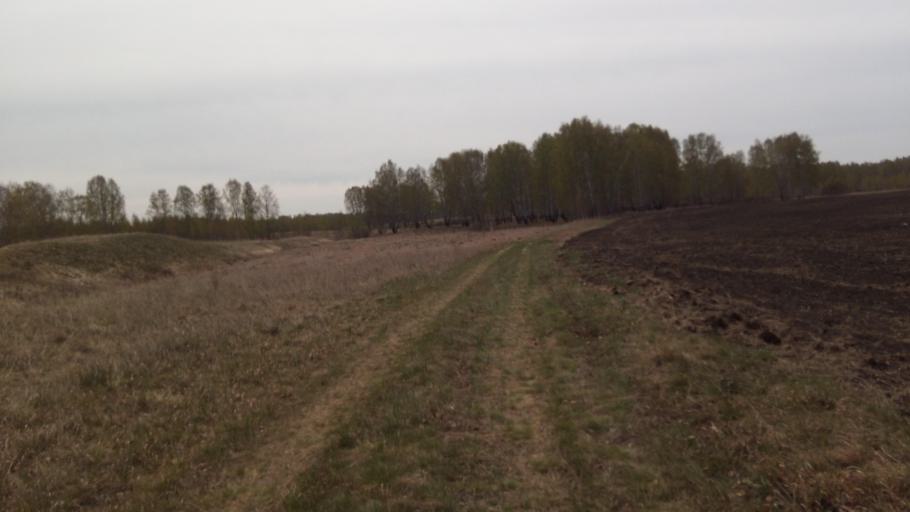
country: RU
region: Chelyabinsk
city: Timiryazevskiy
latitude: 55.0111
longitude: 60.8592
